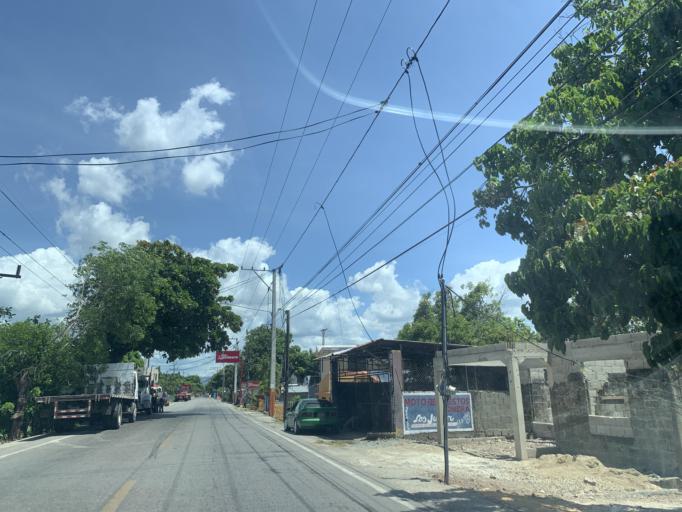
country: DO
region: Puerto Plata
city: Cabarete
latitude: 19.7102
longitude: -70.3848
